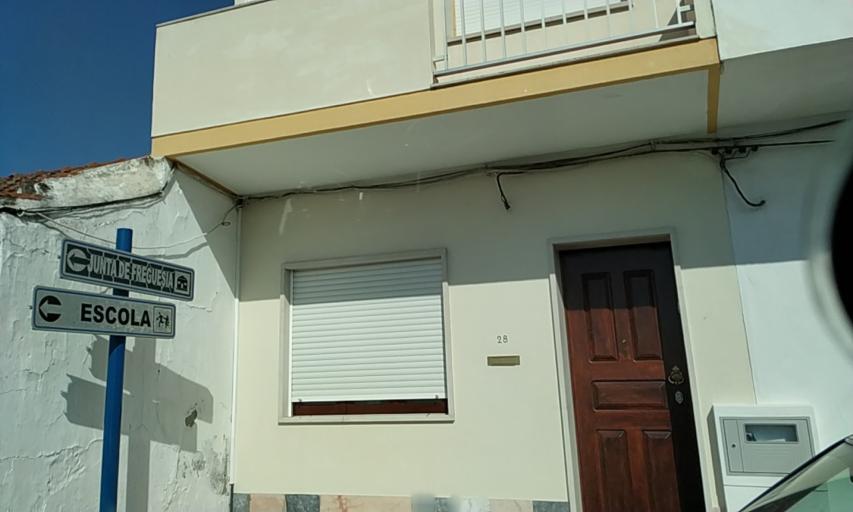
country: PT
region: Santarem
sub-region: Benavente
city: Poceirao
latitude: 38.7666
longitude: -8.6264
